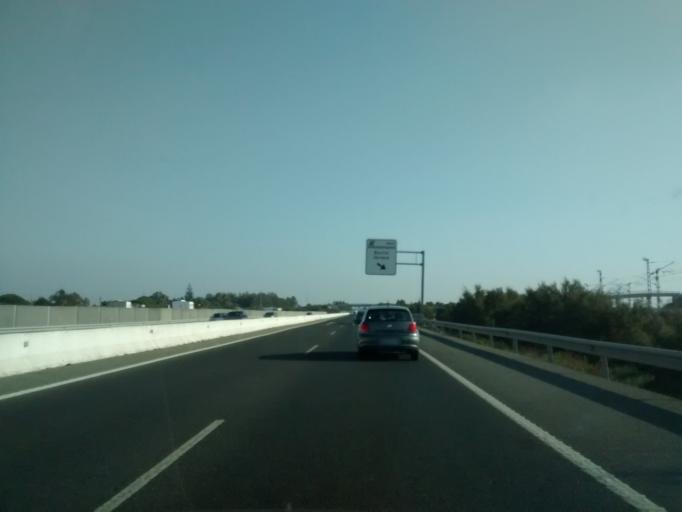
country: ES
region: Andalusia
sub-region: Provincia de Cadiz
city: Puerto Real
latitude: 36.5017
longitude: -6.1447
